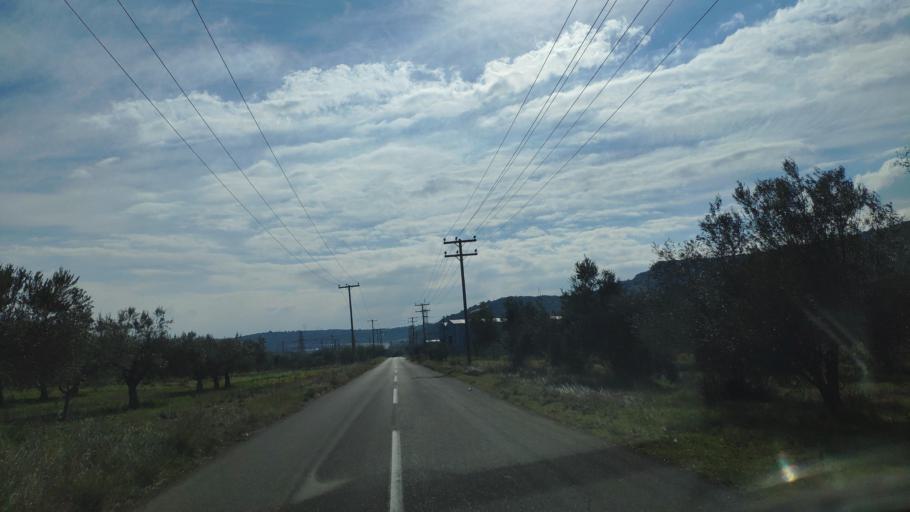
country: GR
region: Central Greece
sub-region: Nomos Evvoias
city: Vathi
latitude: 38.4293
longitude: 23.5914
